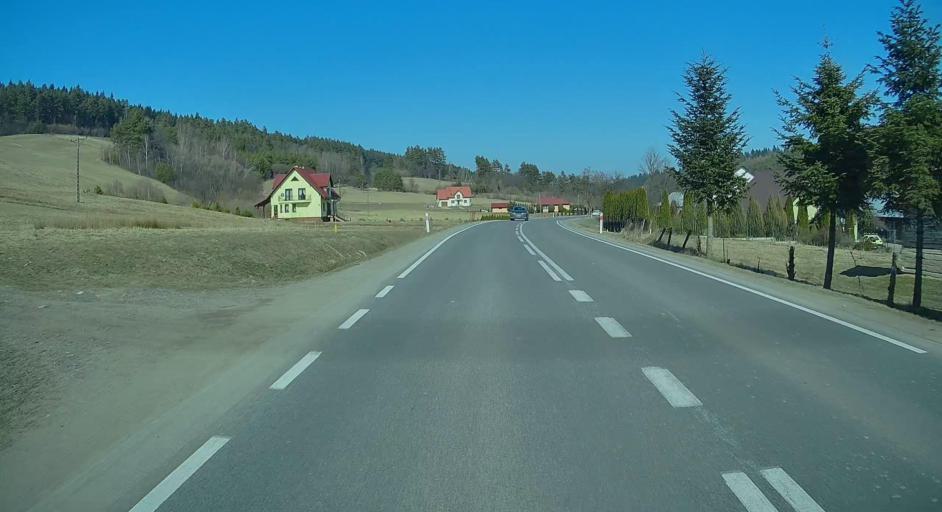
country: PL
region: Subcarpathian Voivodeship
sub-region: Powiat przemyski
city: Bircza
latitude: 49.6747
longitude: 22.4317
